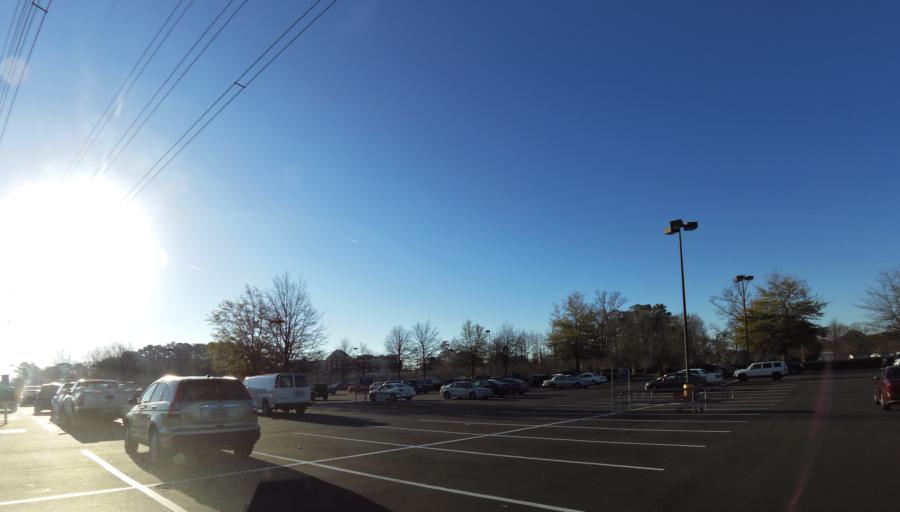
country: US
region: Virginia
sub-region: City of Hampton
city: Hampton
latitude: 37.0381
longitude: -76.3975
